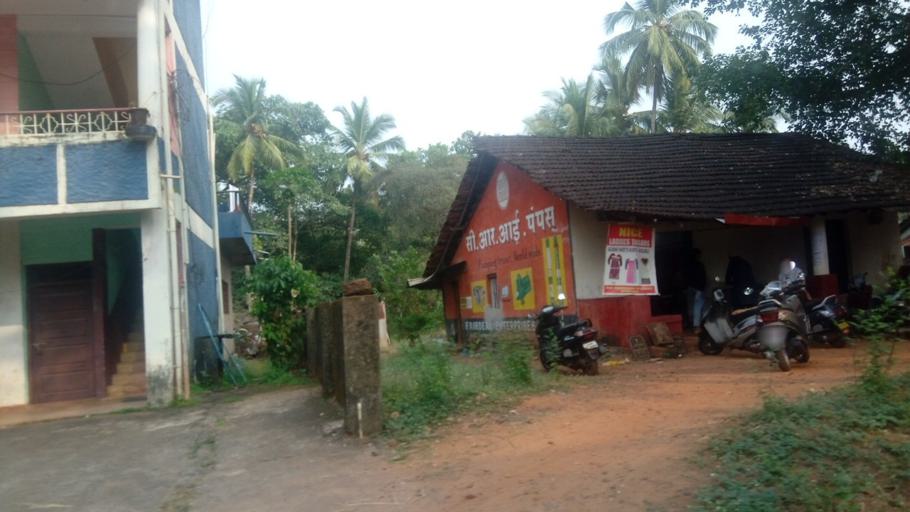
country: IN
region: Goa
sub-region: South Goa
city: Varca
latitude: 15.2371
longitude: 73.9427
